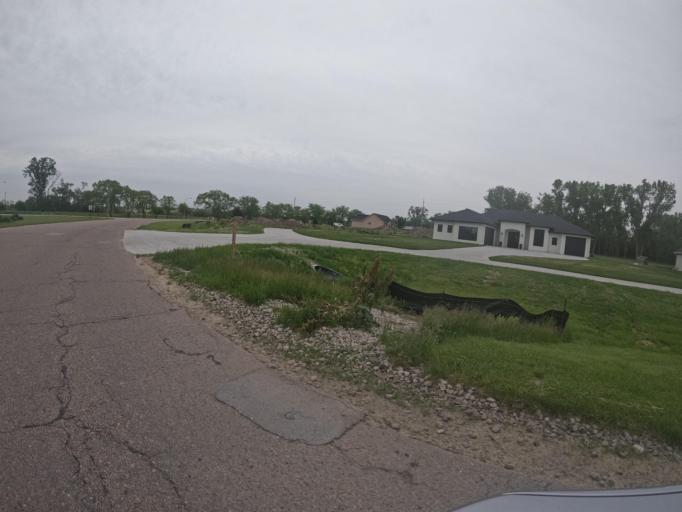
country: US
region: Nebraska
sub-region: Sarpy County
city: Offutt Air Force Base
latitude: 41.0475
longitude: -95.9541
